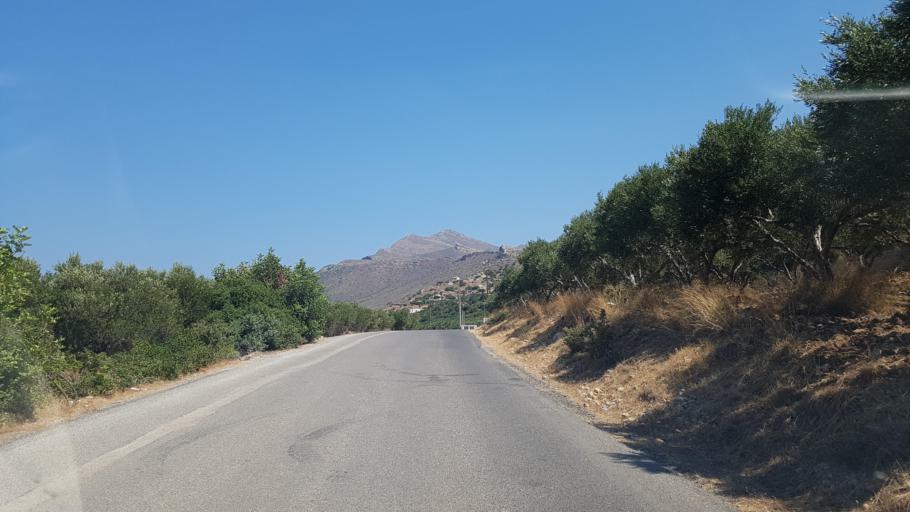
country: GR
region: Crete
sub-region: Nomos Chanias
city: Platanos
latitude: 35.4883
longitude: 23.5887
